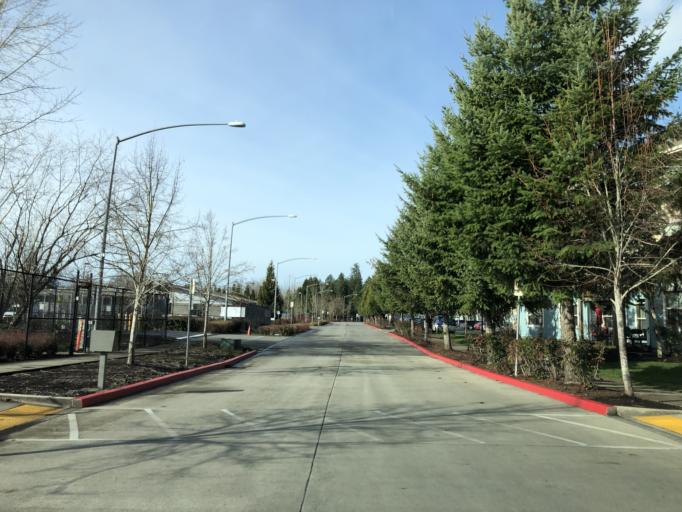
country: US
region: Oregon
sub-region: Washington County
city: Aloha
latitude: 45.5042
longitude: -122.8439
